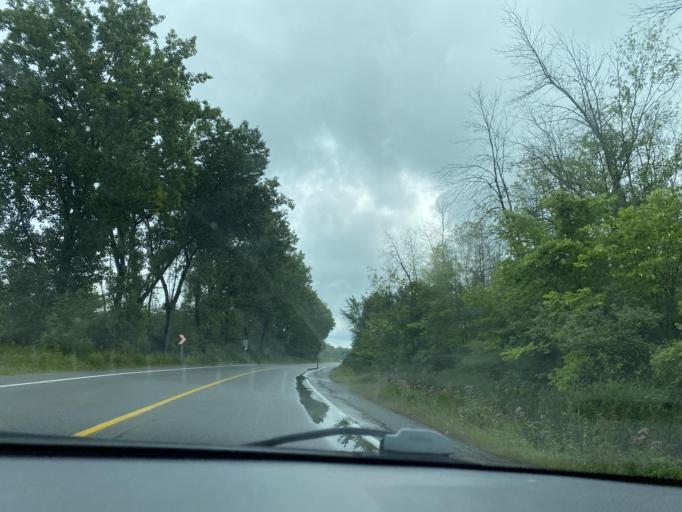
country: CA
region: Quebec
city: Baie-D'Urfe
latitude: 45.4481
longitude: -73.9230
